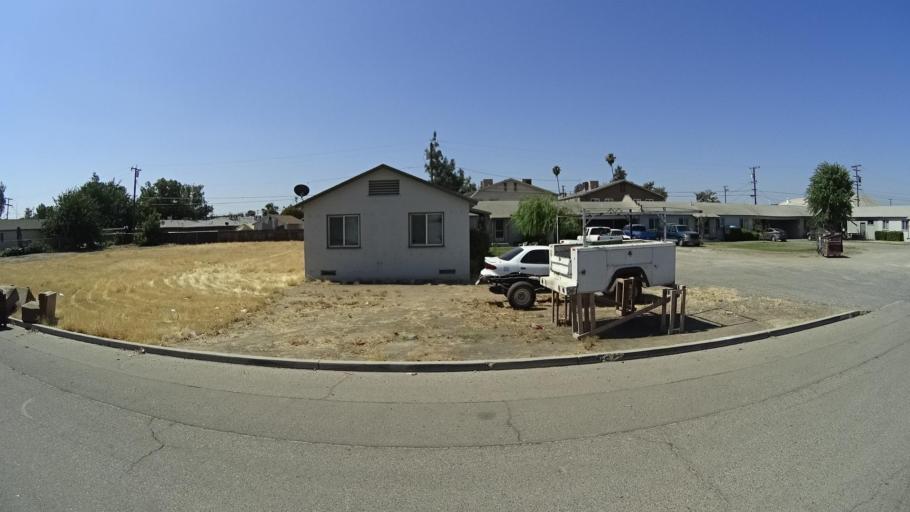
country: US
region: California
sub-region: Fresno County
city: Fresno
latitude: 36.7596
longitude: -119.7784
